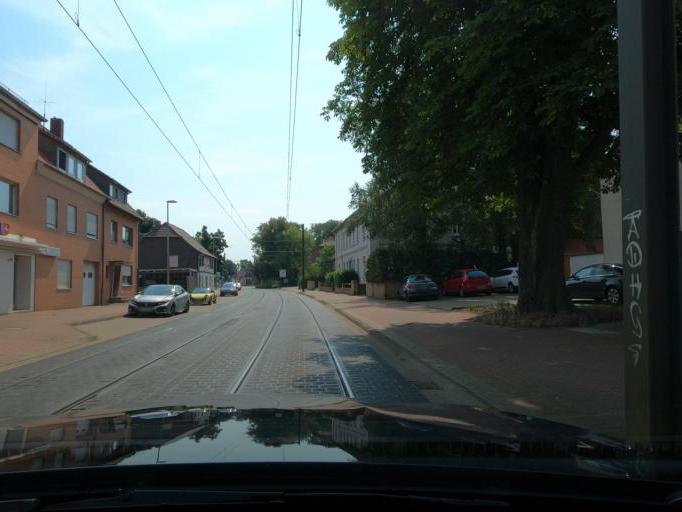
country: DE
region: Lower Saxony
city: Sarstedt
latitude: 52.2718
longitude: 9.8398
